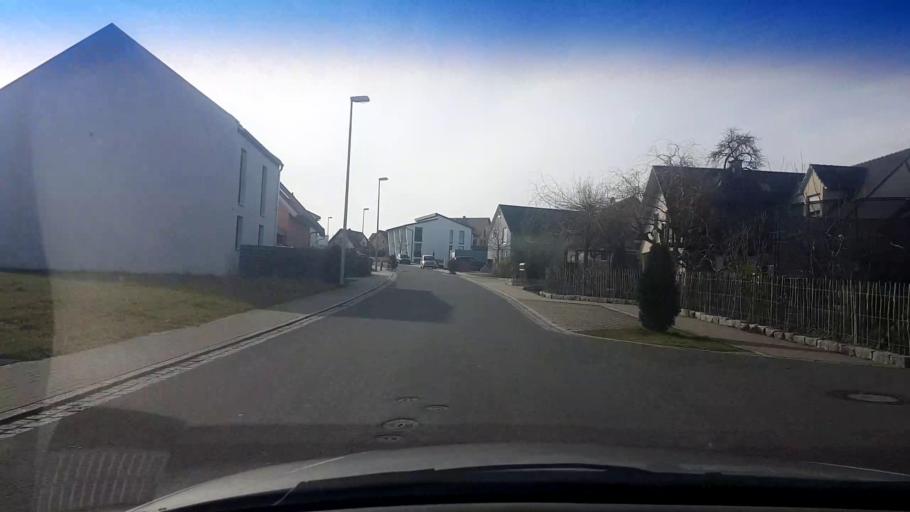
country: DE
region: Bavaria
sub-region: Upper Franconia
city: Burgebrach
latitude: 49.8211
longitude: 10.7434
